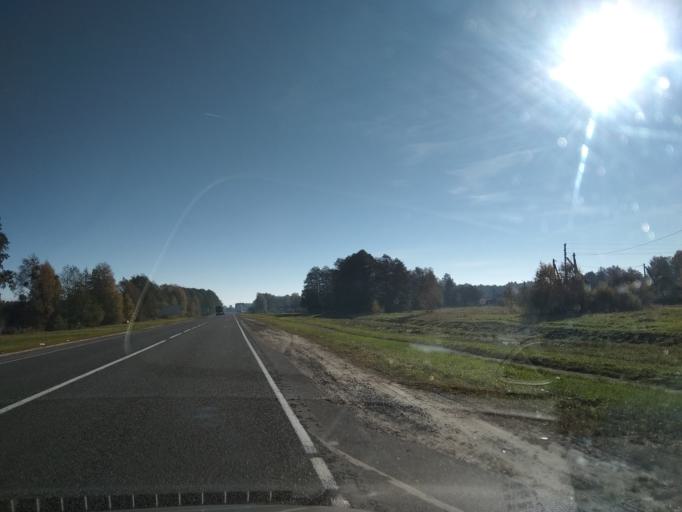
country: BY
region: Brest
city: Malaryta
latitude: 51.8314
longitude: 24.2781
